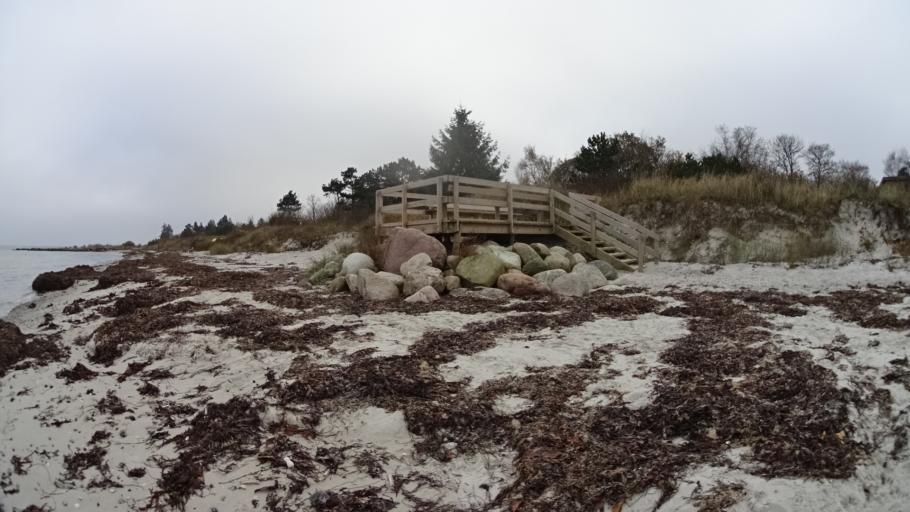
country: DK
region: Central Jutland
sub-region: Arhus Kommune
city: Malling
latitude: 55.9693
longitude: 10.2586
